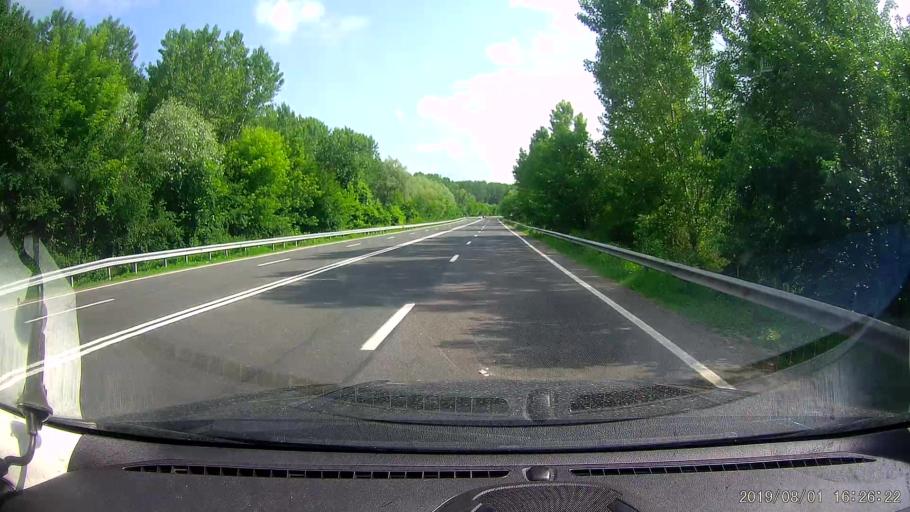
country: RO
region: Calarasi
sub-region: Municipiul Calarasi
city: Calarasi
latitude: 44.1816
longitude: 27.3218
